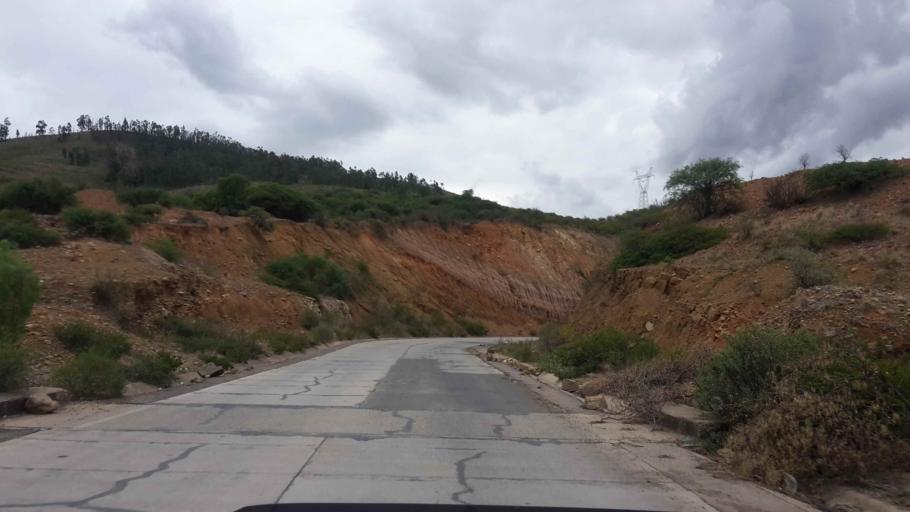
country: BO
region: Cochabamba
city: Cochabamba
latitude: -17.5315
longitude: -66.2011
